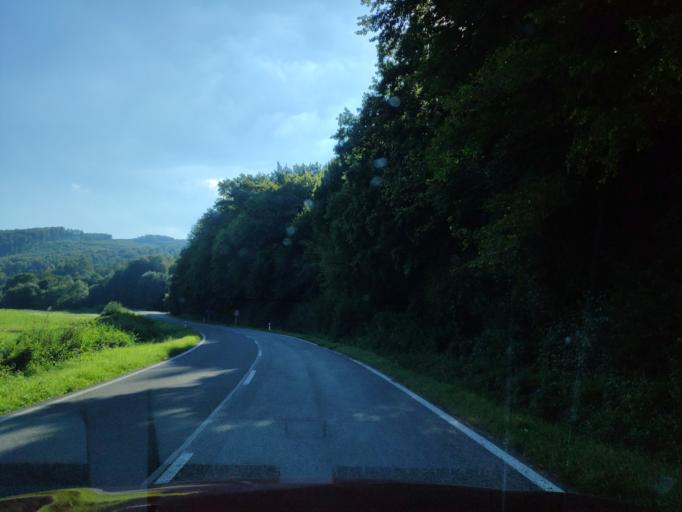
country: SK
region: Presovsky
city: Snina
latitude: 49.0371
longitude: 22.2518
